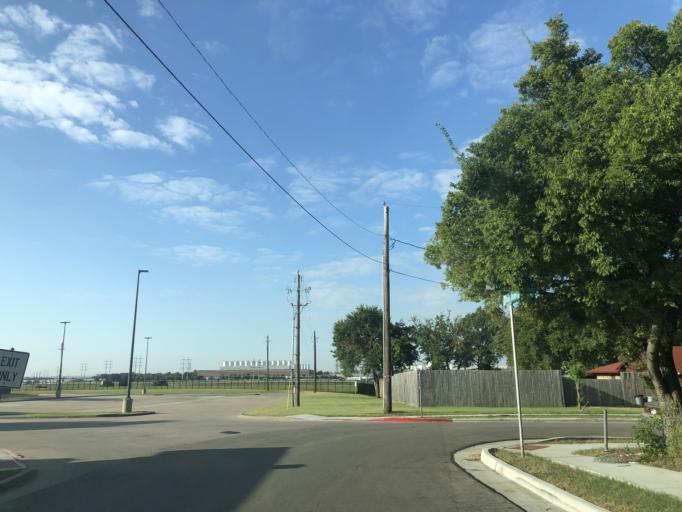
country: US
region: Texas
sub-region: Dallas County
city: Grand Prairie
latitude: 32.7333
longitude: -97.0310
